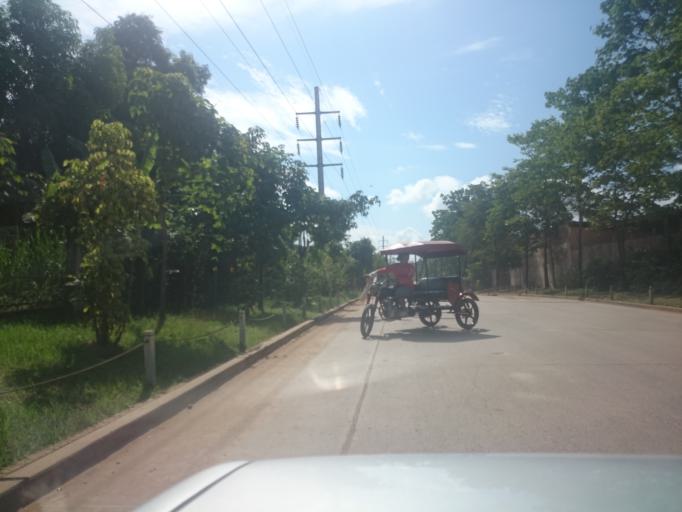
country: PE
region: Ucayali
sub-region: Provincia de Coronel Portillo
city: Puerto Callao
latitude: -8.3564
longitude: -74.5765
